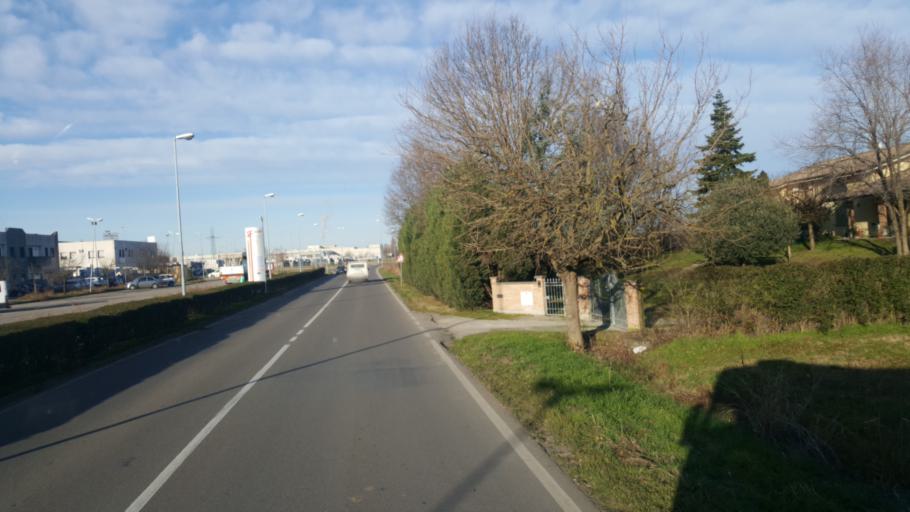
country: IT
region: Emilia-Romagna
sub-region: Provincia di Reggio Emilia
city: Rubiera
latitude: 44.6586
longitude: 10.7780
